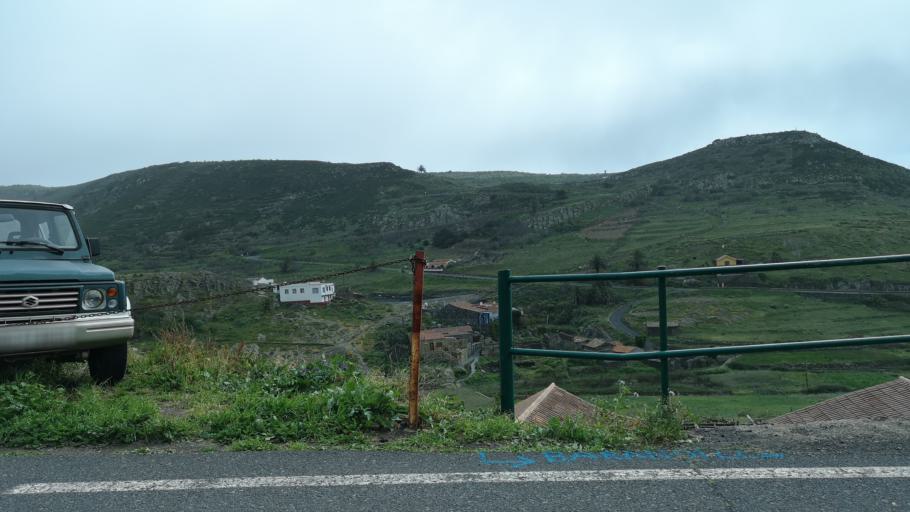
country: ES
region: Canary Islands
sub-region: Provincia de Santa Cruz de Tenerife
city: Vallehermosa
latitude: 28.1352
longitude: -17.3186
